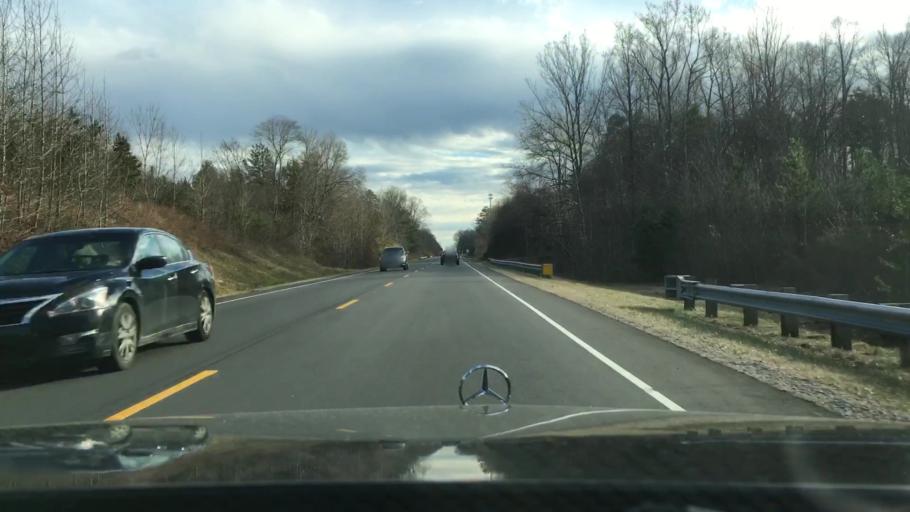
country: US
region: Virginia
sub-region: City of Danville
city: Danville
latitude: 36.4980
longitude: -79.3865
